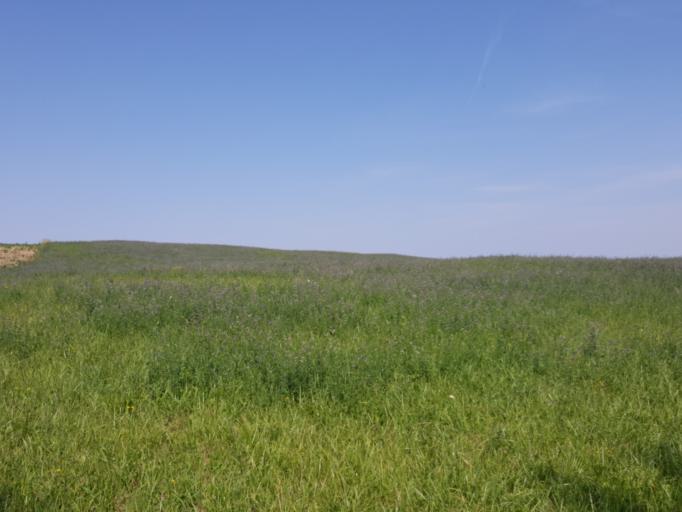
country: LT
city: Vilkaviskis
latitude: 54.4343
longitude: 22.9911
